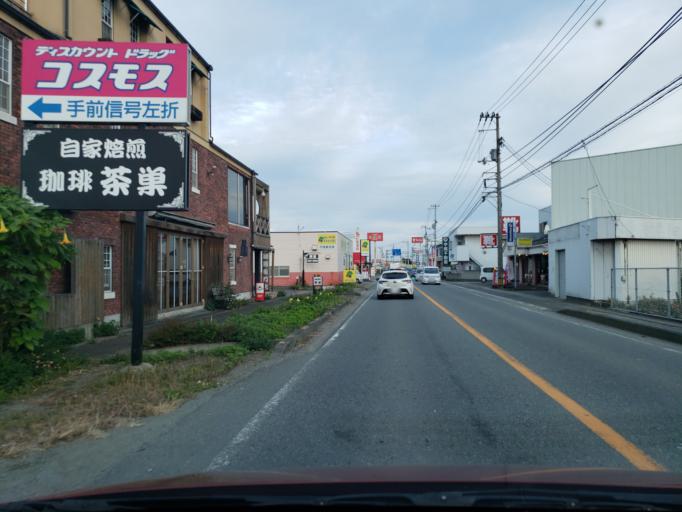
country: JP
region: Tokushima
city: Kamojimacho-jogejima
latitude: 34.0841
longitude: 134.2791
